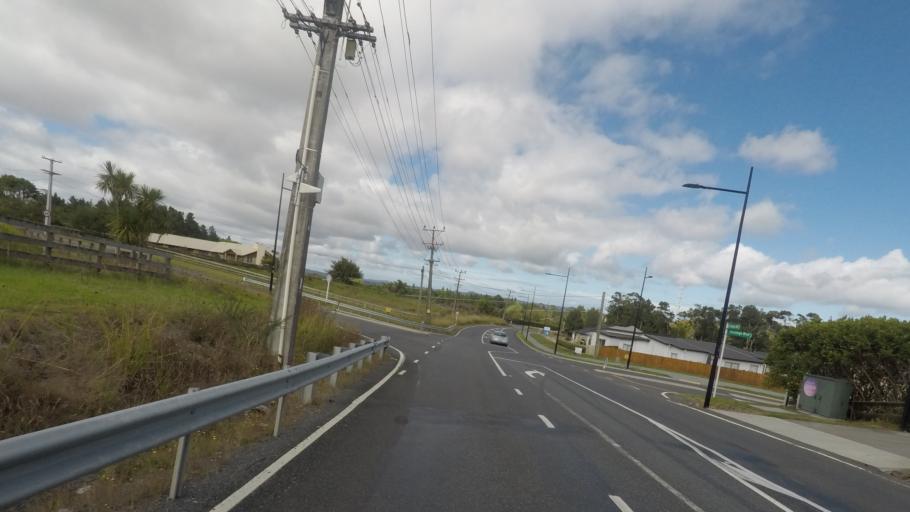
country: NZ
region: Auckland
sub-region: Auckland
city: Muriwai Beach
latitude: -36.7671
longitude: 174.5558
